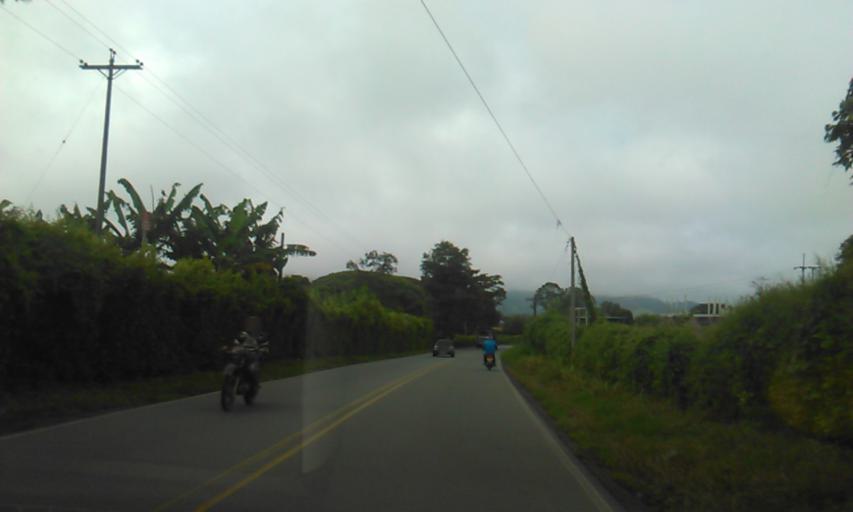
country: CO
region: Quindio
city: Cordoba
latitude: 4.4184
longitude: -75.7231
